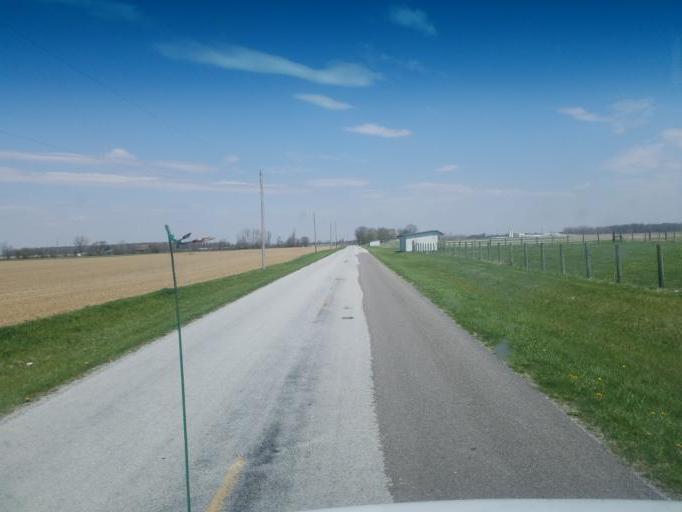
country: US
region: Ohio
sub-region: Hardin County
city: Forest
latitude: 40.7546
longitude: -83.5378
